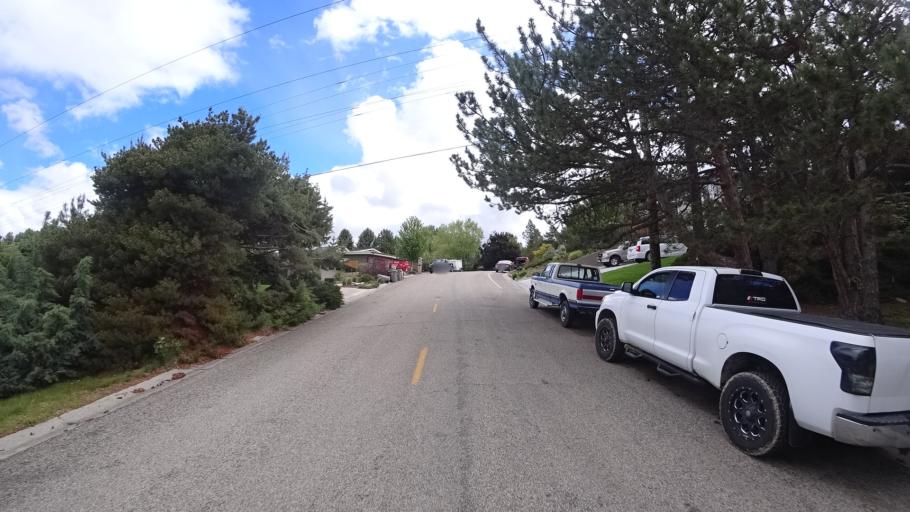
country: US
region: Idaho
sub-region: Ada County
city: Boise
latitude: 43.6470
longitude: -116.1864
